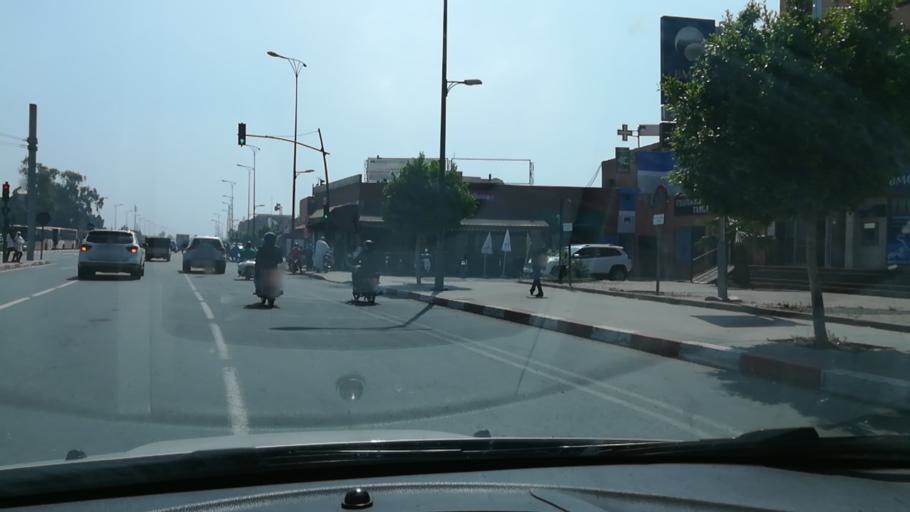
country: MA
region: Marrakech-Tensift-Al Haouz
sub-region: Marrakech
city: Marrakesh
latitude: 31.6274
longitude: -8.0432
